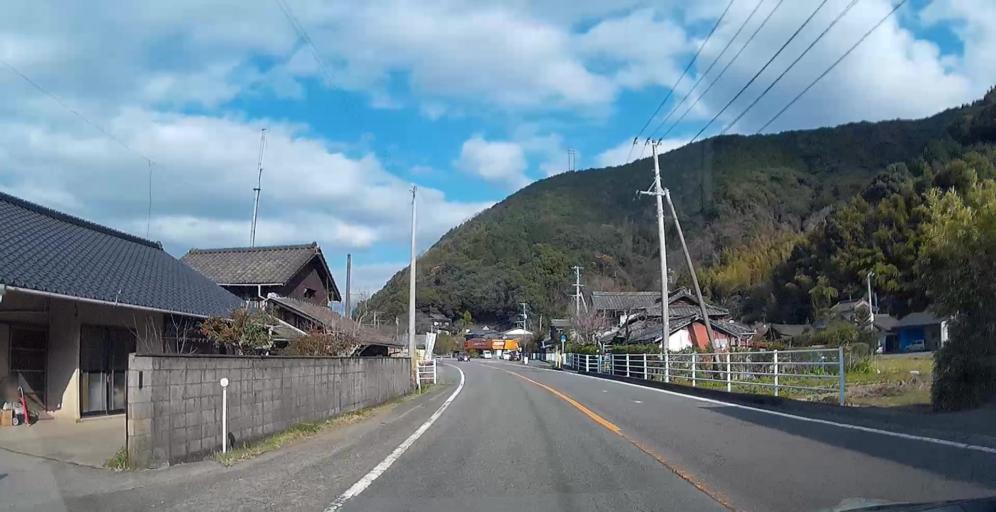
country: JP
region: Kumamoto
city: Yatsushiro
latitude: 32.4227
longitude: 130.5554
